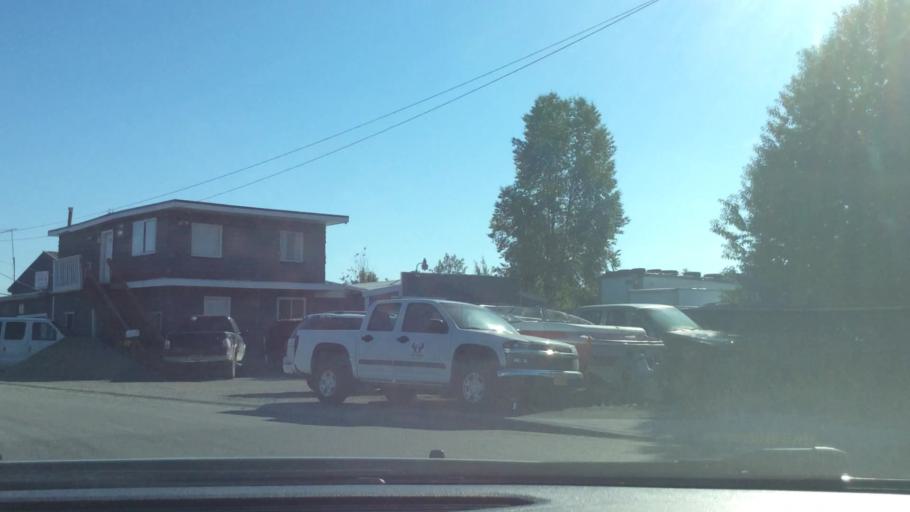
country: US
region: Alaska
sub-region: Anchorage Municipality
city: Anchorage
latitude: 61.1662
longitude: -149.8459
